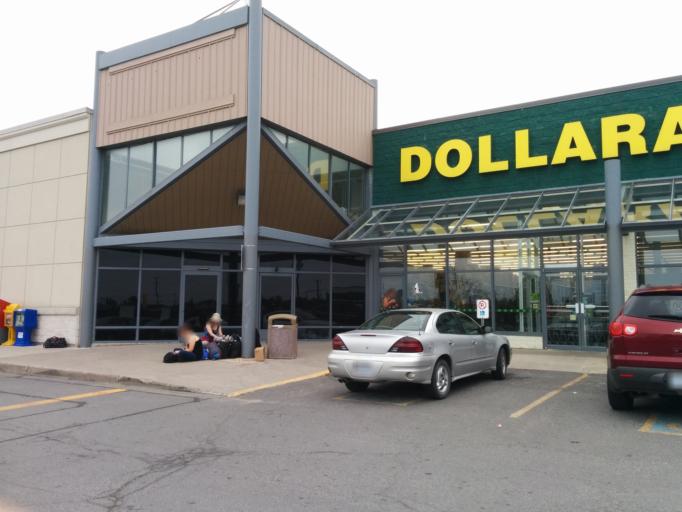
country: CA
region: Ontario
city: Kingston
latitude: 44.2658
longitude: -76.4969
